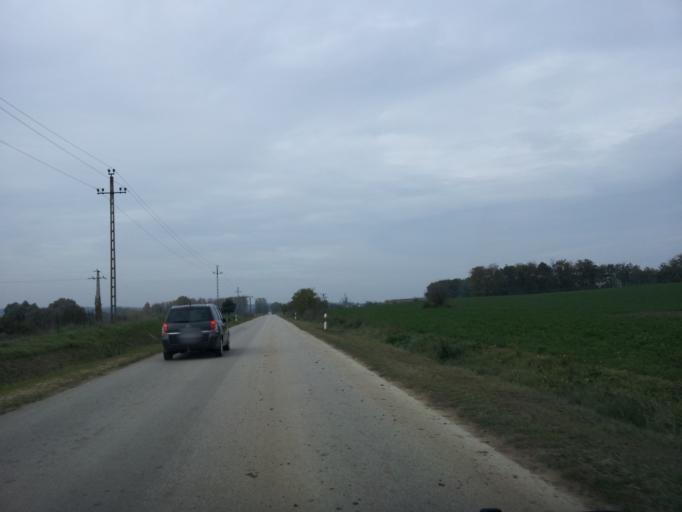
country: HU
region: Gyor-Moson-Sopron
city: Bakonyszentlaszlo
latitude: 47.4234
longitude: 17.8013
